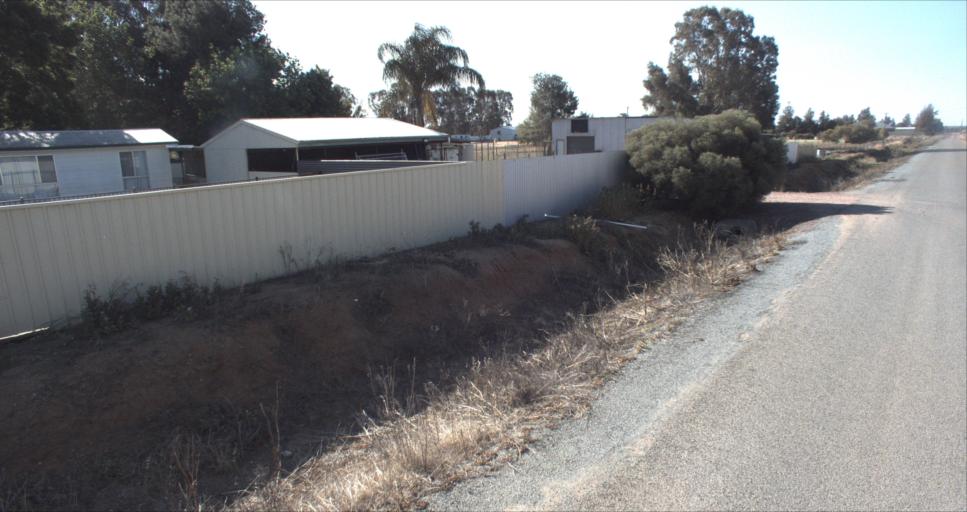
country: AU
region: New South Wales
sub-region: Leeton
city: Leeton
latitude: -34.5404
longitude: 146.4157
